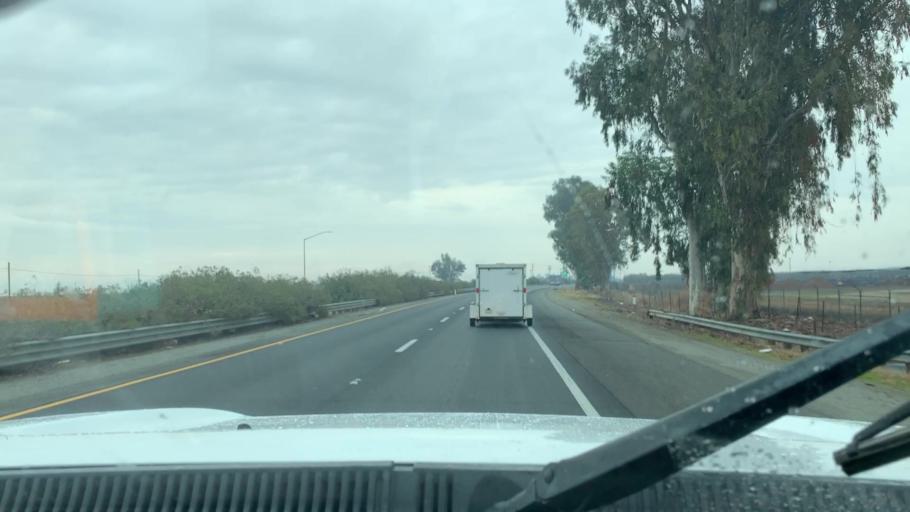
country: US
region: California
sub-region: Kern County
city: Delano
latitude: 35.8155
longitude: -119.2581
